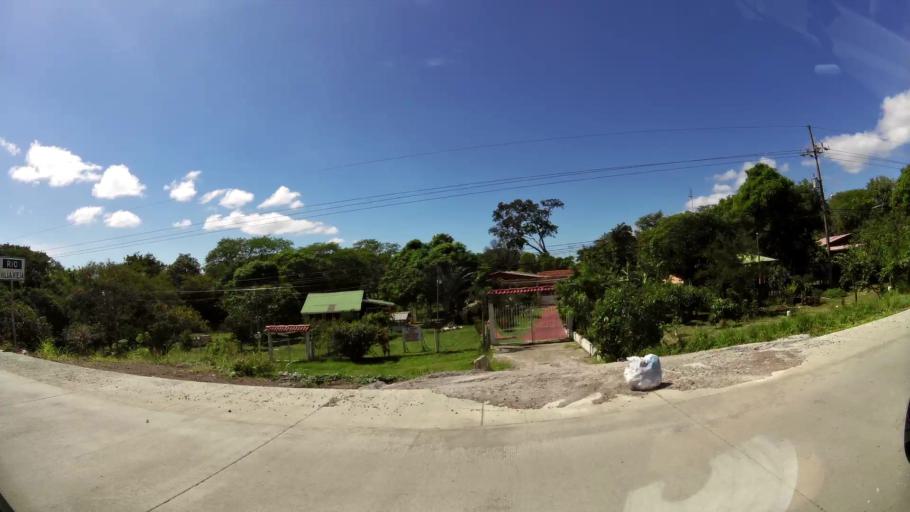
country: CR
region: Guanacaste
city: Bagaces
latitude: 10.5022
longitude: -85.2307
